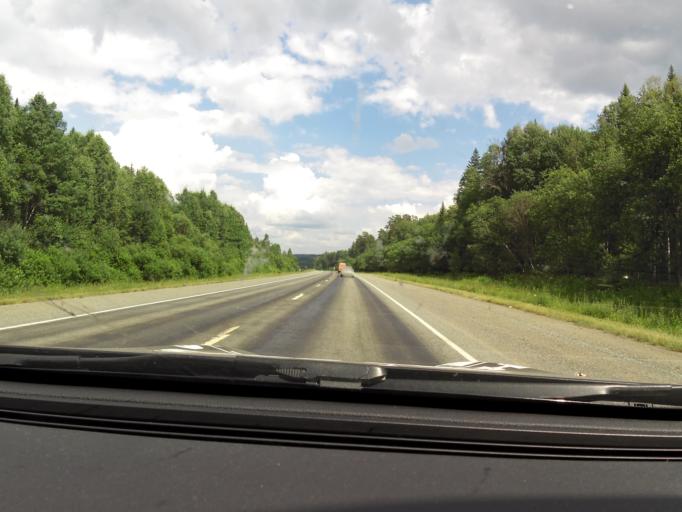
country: RU
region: Sverdlovsk
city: Bisert'
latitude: 56.8319
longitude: 58.8173
